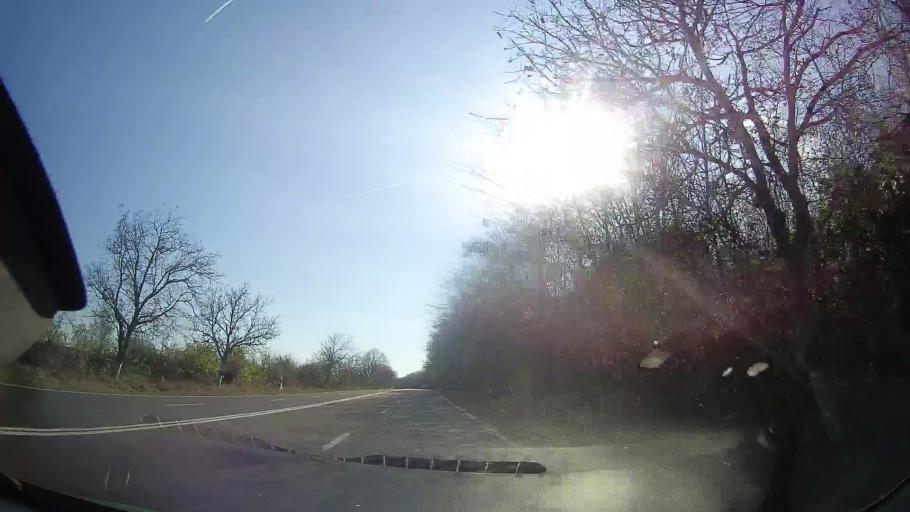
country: RO
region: Constanta
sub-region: Comuna Douazeci si Trei August
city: Dulcesti
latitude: 43.8860
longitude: 28.5732
